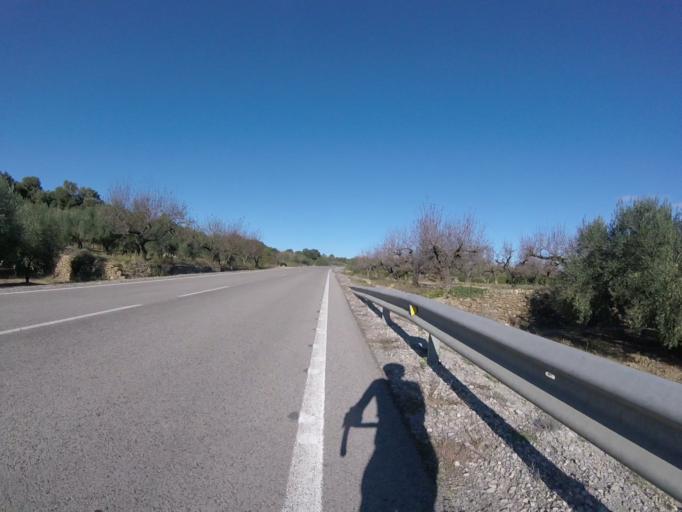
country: ES
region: Valencia
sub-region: Provincia de Castello
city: Cervera del Maestre
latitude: 40.4700
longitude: 0.2437
